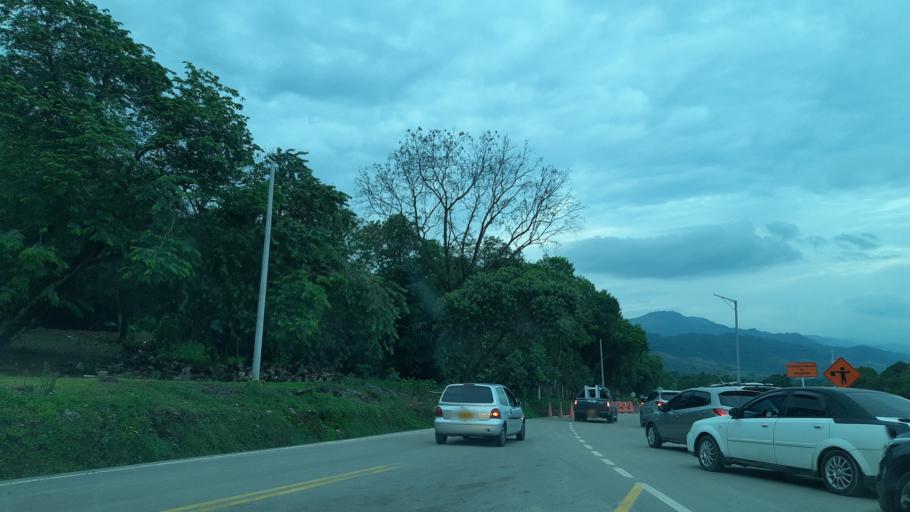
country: CO
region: Casanare
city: Sabanalarga
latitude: 4.7545
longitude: -73.0093
